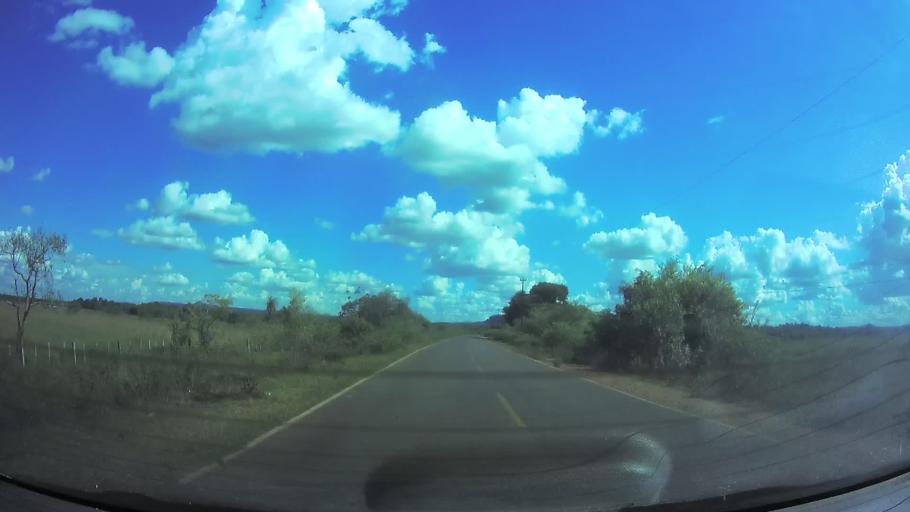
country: PY
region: Paraguari
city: Sapucai
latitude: -25.6764
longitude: -56.8620
